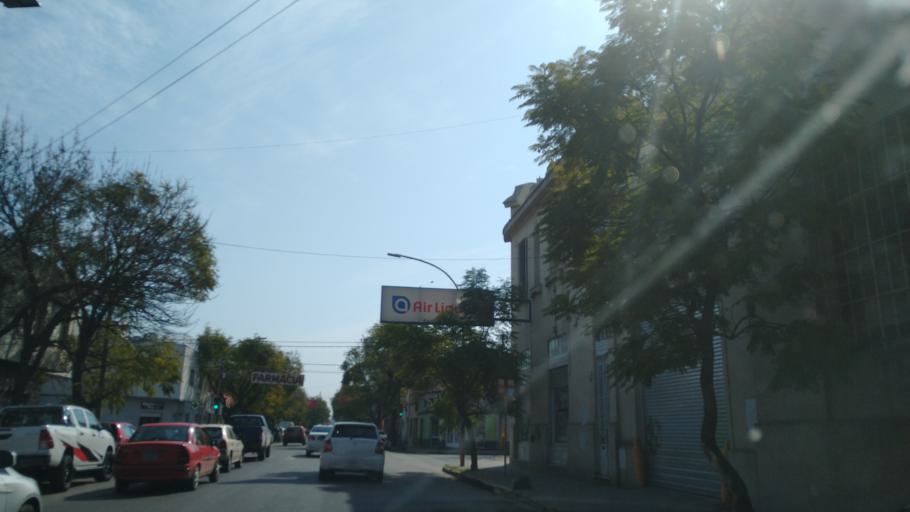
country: AR
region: Buenos Aires
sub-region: Partido de Bahia Blanca
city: Bahia Blanca
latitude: -38.7296
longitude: -62.2555
